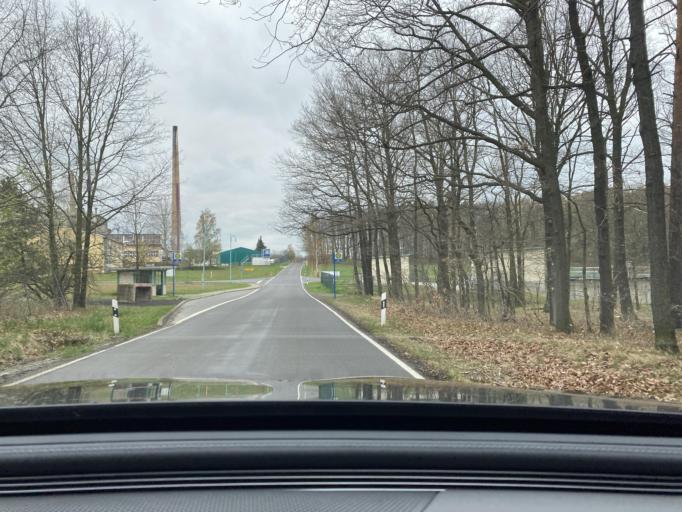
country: DE
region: Saxony
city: Puschwitz
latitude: 51.2576
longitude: 14.3019
